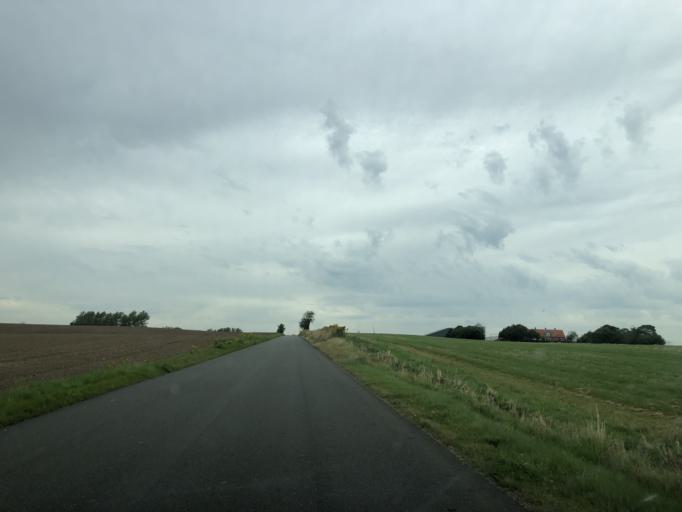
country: DK
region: Central Jutland
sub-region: Holstebro Kommune
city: Holstebro
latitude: 56.3912
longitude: 8.5973
